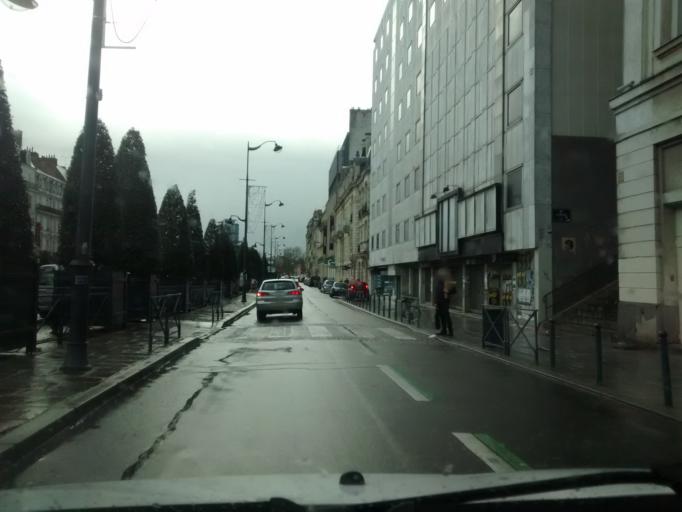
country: FR
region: Brittany
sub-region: Departement d'Ille-et-Vilaine
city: Rennes
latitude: 48.1102
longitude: -1.6809
